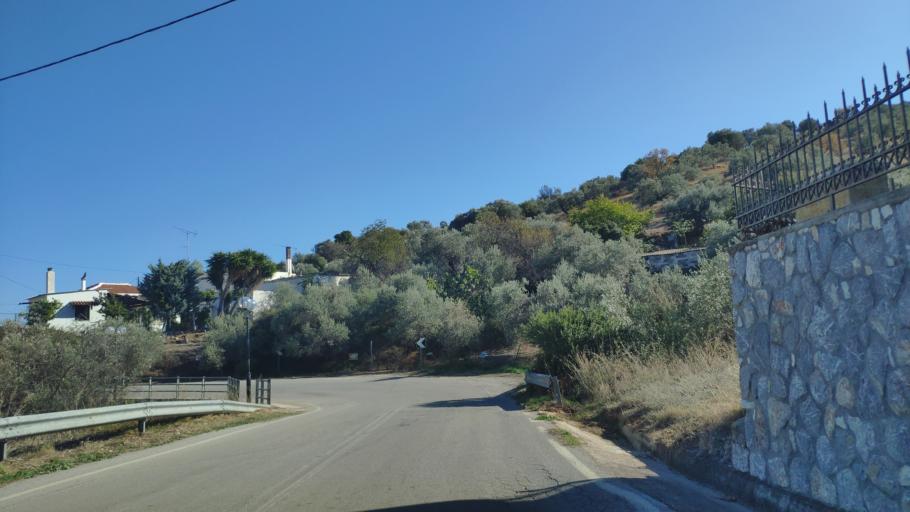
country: GR
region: Attica
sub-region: Nomos Piraios
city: Galatas
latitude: 37.5428
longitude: 23.3695
